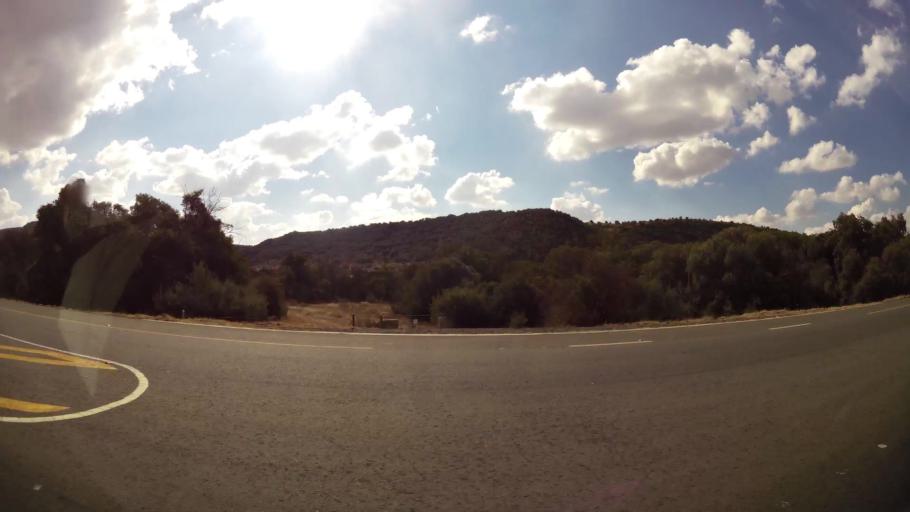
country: ZA
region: Orange Free State
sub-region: Mangaung Metropolitan Municipality
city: Bloemfontein
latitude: -29.1593
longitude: 26.0502
